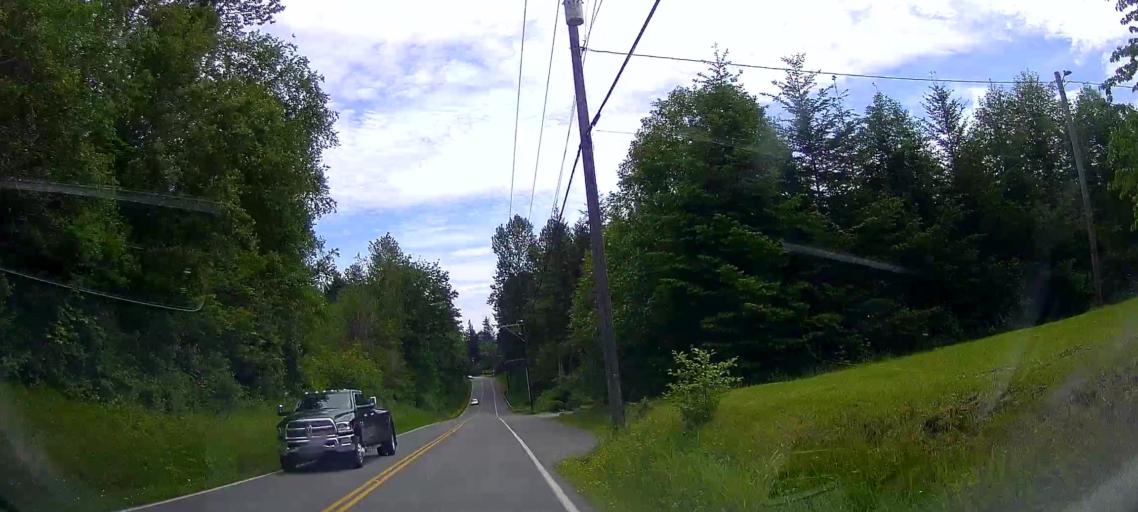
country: US
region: Washington
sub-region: Snohomish County
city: Bryant
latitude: 48.2388
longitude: -122.2303
